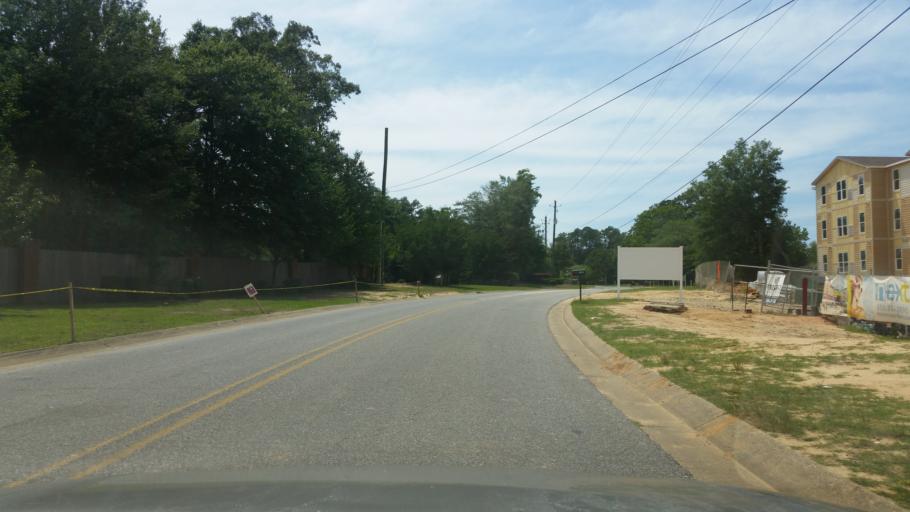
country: US
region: Florida
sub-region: Escambia County
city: Ferry Pass
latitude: 30.5396
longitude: -87.2146
